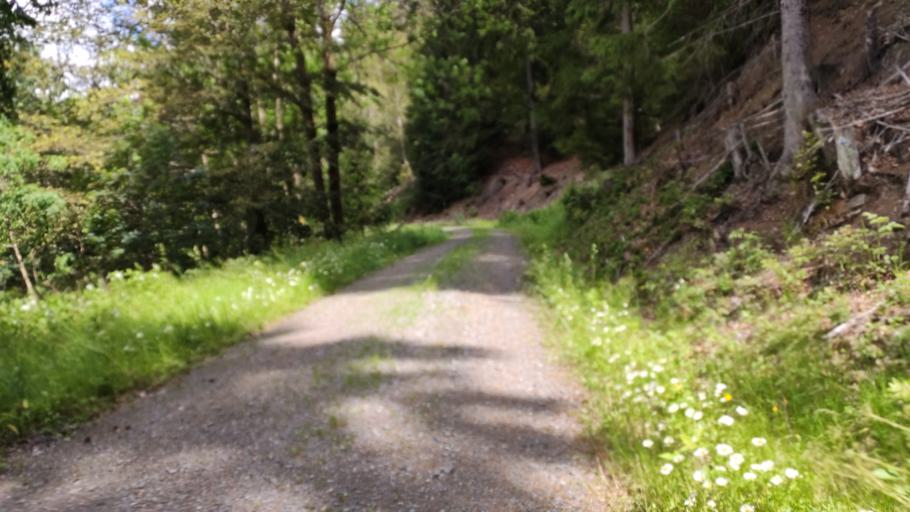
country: DE
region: Bavaria
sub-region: Upper Franconia
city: Tschirn
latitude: 50.3787
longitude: 11.4670
